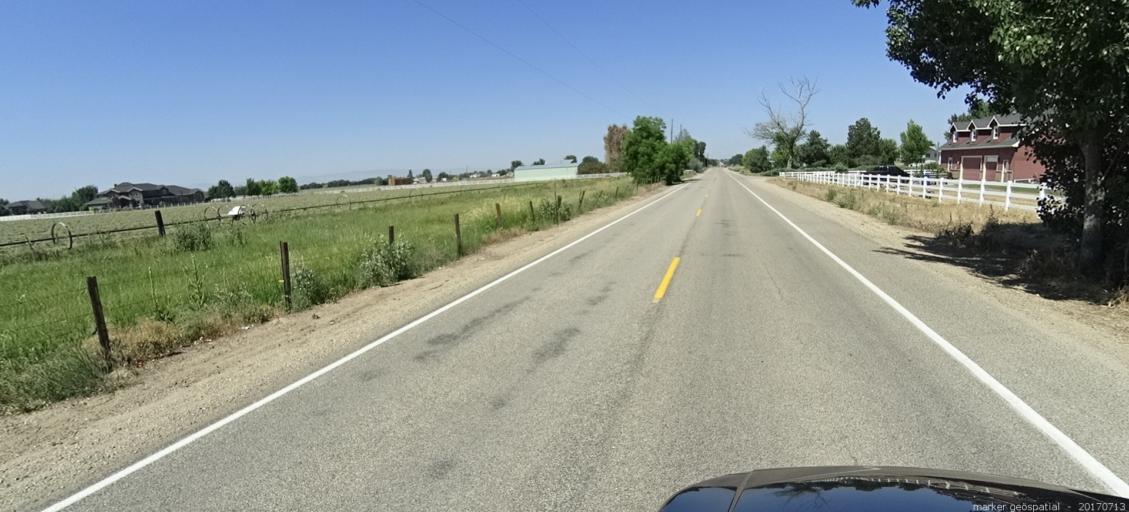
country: US
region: Idaho
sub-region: Ada County
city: Kuna
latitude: 43.5319
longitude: -116.3868
